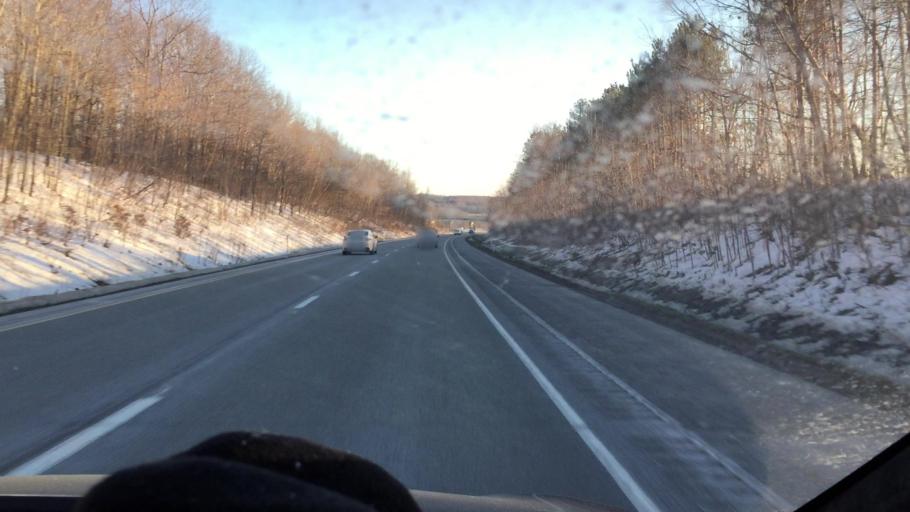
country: US
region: Pennsylvania
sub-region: Crawford County
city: Meadville
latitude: 41.7045
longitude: -80.1996
